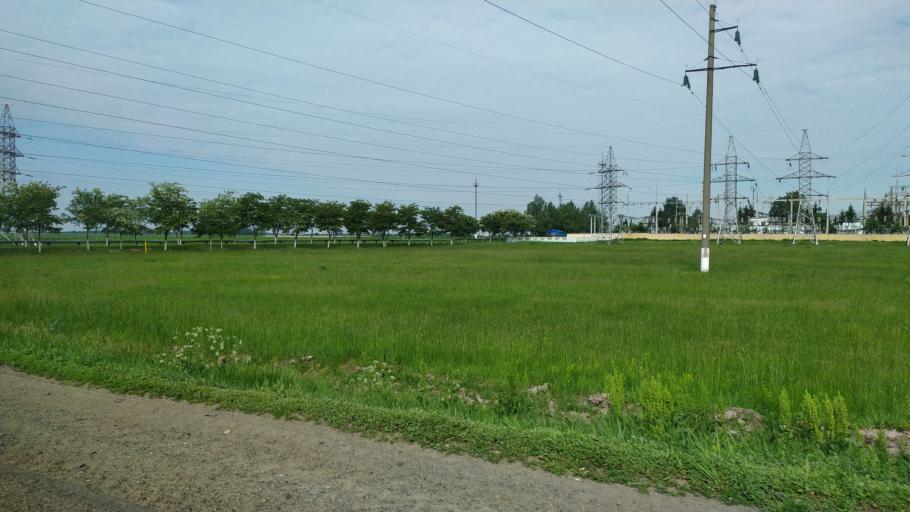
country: BY
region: Gomel
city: Gomel
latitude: 52.4561
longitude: 30.9010
